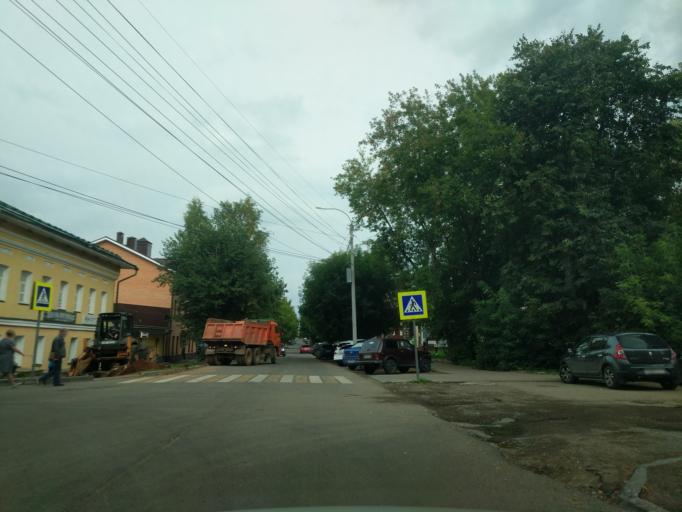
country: RU
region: Kirov
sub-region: Kirovo-Chepetskiy Rayon
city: Kirov
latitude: 58.5963
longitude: 49.6852
